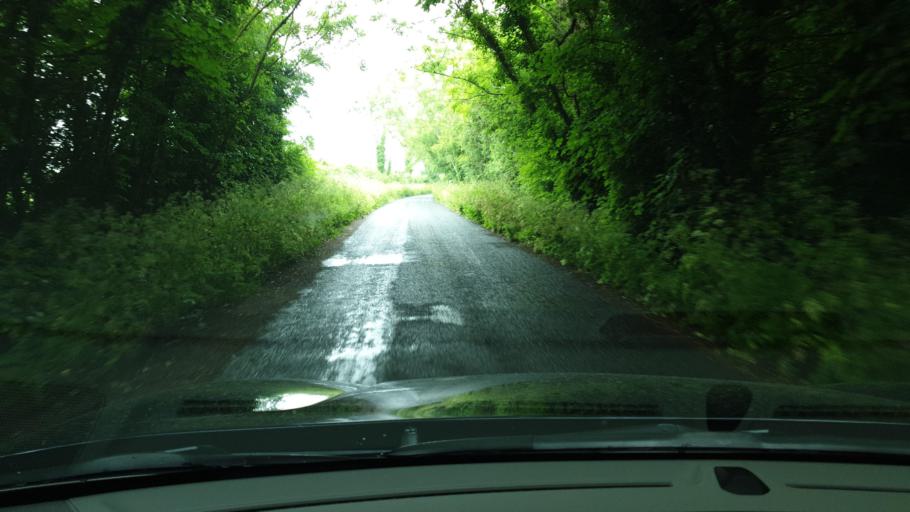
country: IE
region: Leinster
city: Hartstown
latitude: 53.4233
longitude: -6.4215
